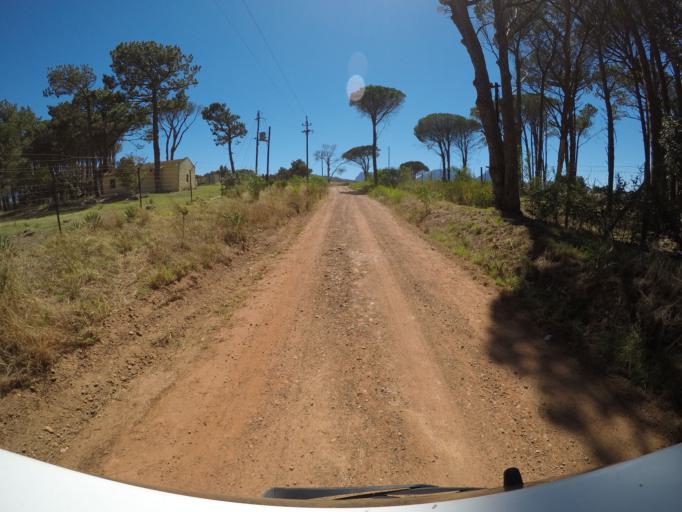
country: ZA
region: Western Cape
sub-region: Overberg District Municipality
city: Grabouw
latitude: -34.1156
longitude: 18.8790
